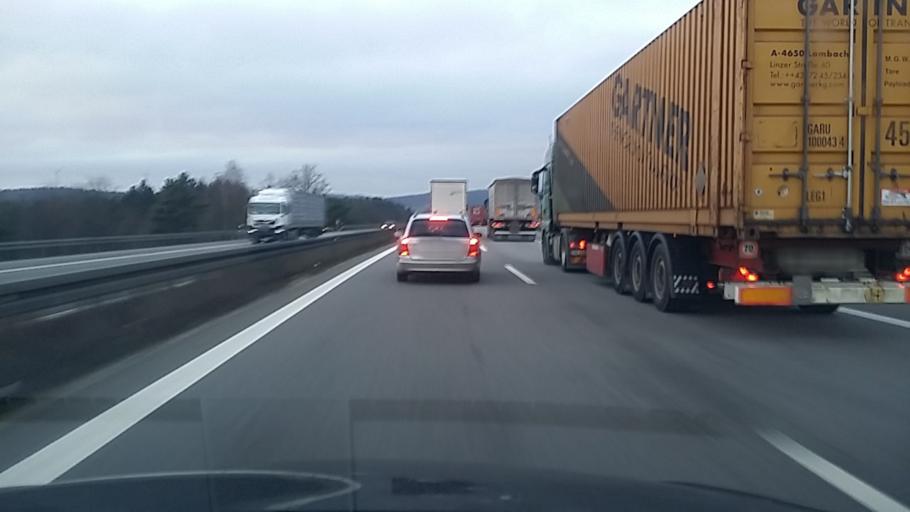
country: DE
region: Bavaria
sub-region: Upper Palatinate
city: Hohenfels
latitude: 49.1508
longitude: 11.8456
